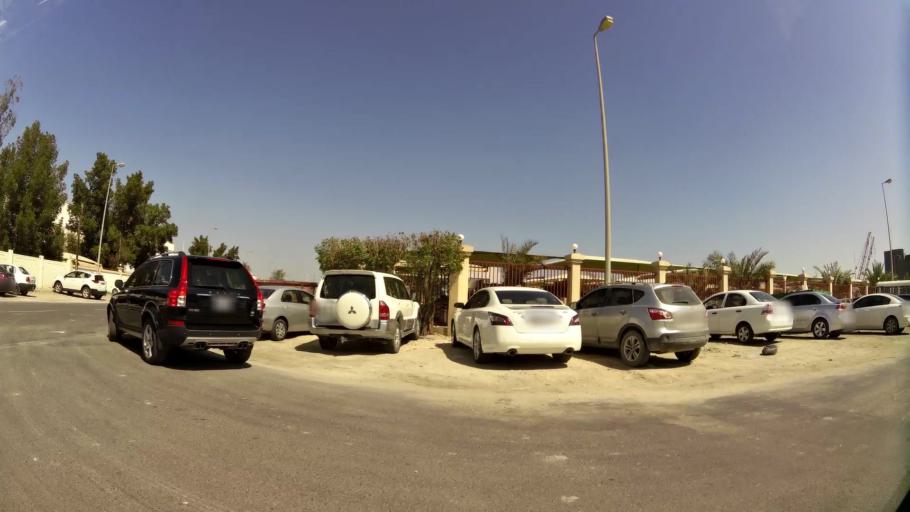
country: BH
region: Manama
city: Manama
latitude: 26.1973
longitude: 50.5953
